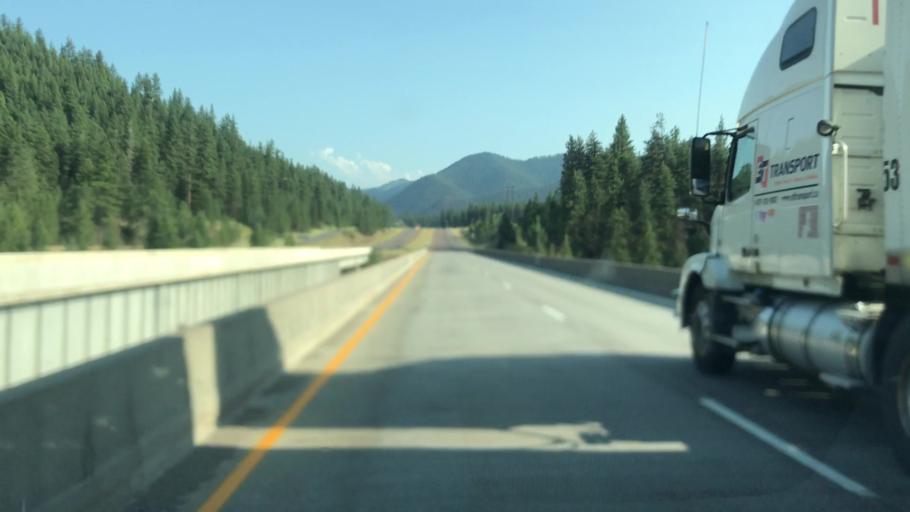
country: US
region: Montana
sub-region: Mineral County
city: Superior
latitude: 47.0686
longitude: -114.7647
